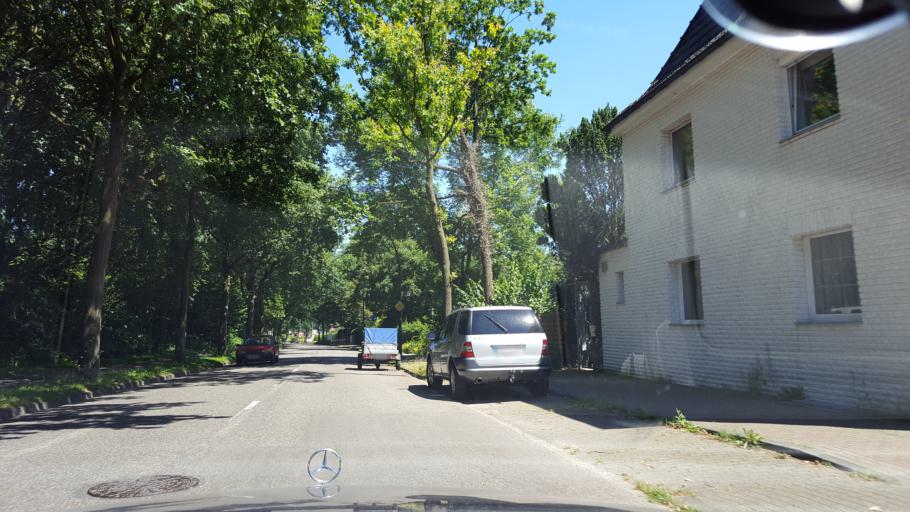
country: DE
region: North Rhine-Westphalia
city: Marl
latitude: 51.6568
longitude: 7.1218
